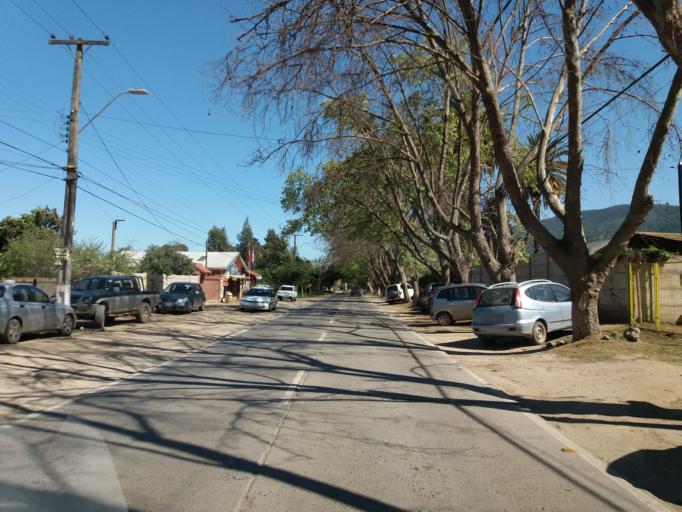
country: CL
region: Valparaiso
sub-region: Provincia de Marga Marga
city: Limache
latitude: -32.9986
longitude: -71.2164
